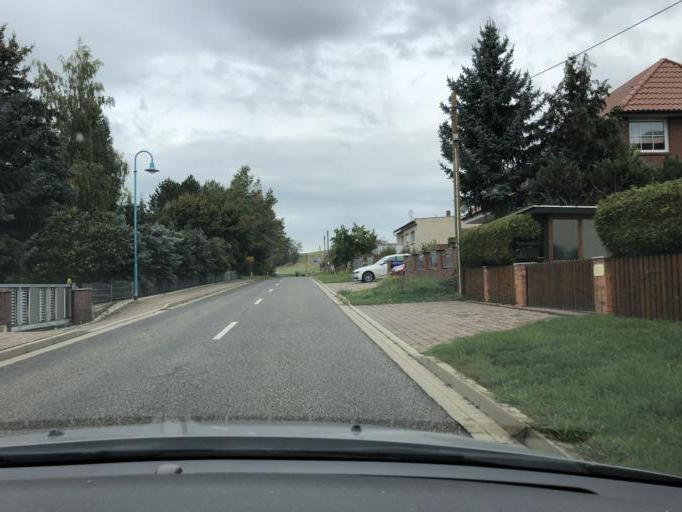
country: DE
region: Saxony-Anhalt
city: Uichteritz
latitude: 51.2101
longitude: 11.9141
